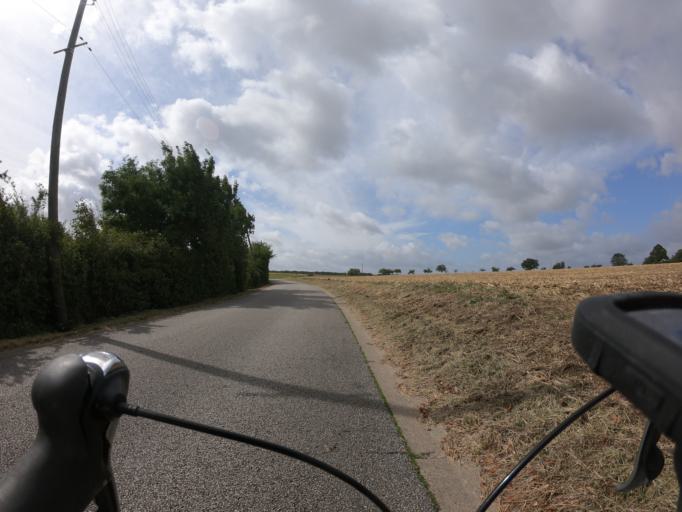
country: FR
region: Ile-de-France
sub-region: Departement des Yvelines
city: Magny-les-Hameaux
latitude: 48.7448
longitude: 2.0550
